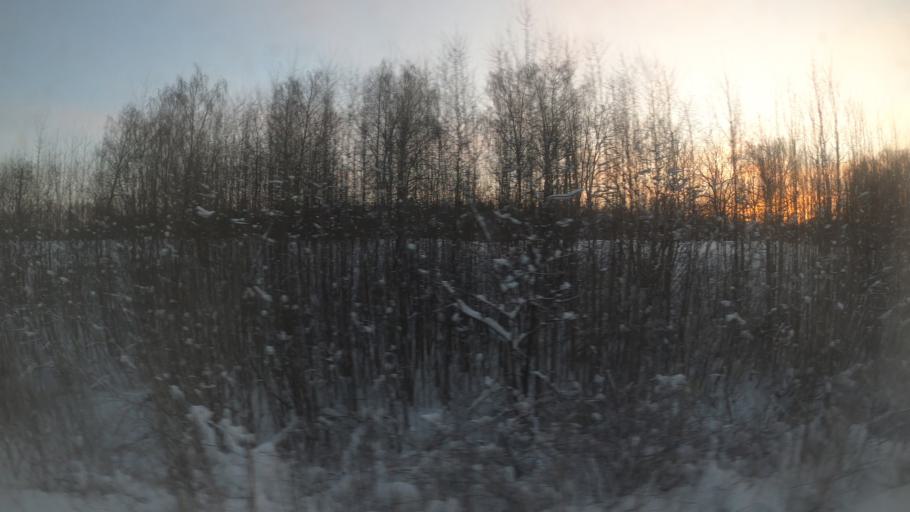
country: RU
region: Moskovskaya
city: Podosinki
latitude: 56.2175
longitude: 37.5272
